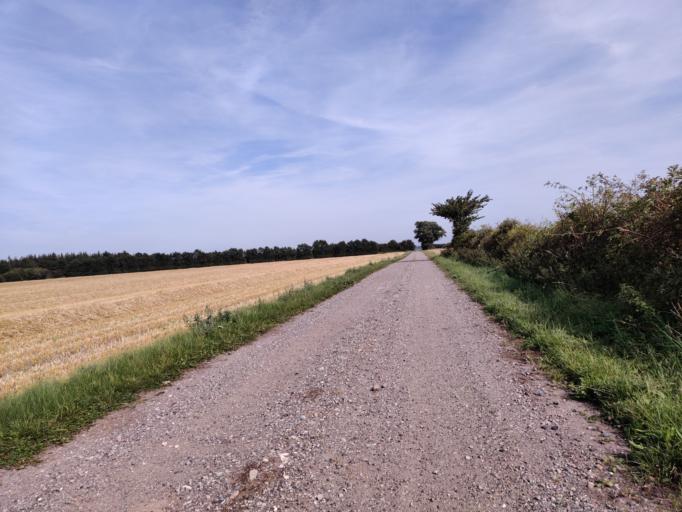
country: DK
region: Zealand
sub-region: Guldborgsund Kommune
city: Nykobing Falster
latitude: 54.6439
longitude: 11.9069
